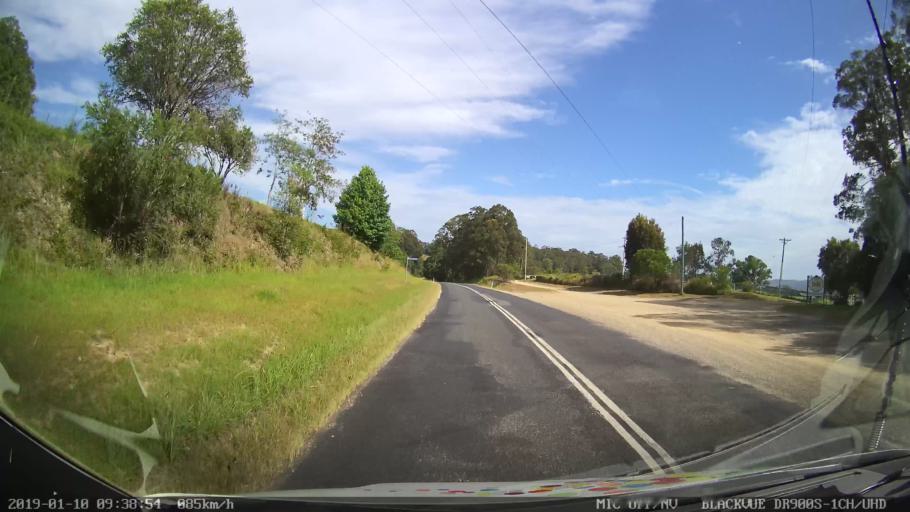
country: AU
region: New South Wales
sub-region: Coffs Harbour
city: Nana Glen
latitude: -30.1696
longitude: 153.0055
